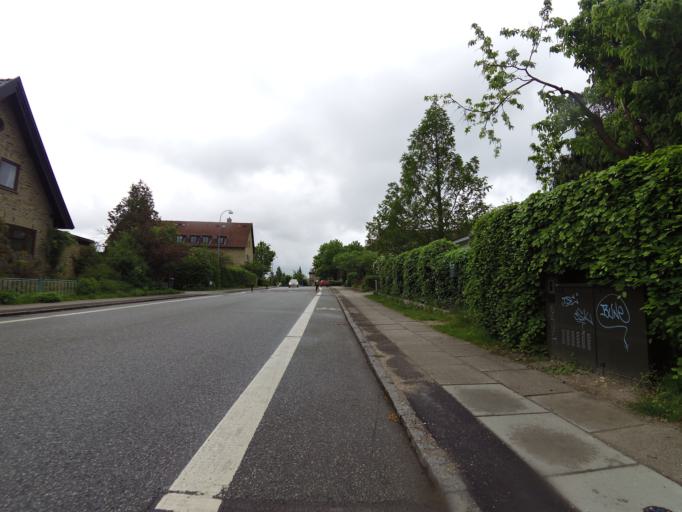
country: DK
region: Capital Region
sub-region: Gladsaxe Municipality
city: Buddinge
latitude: 55.7245
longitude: 12.5107
